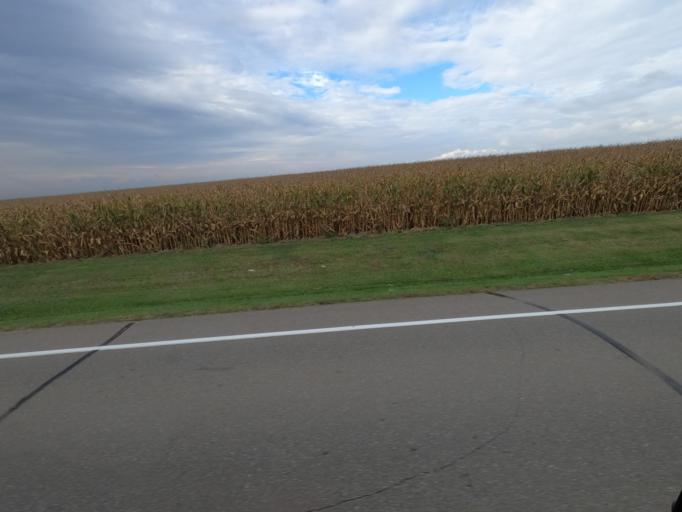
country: US
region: Iowa
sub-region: Henry County
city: Mount Pleasant
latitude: 40.7845
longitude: -91.5793
